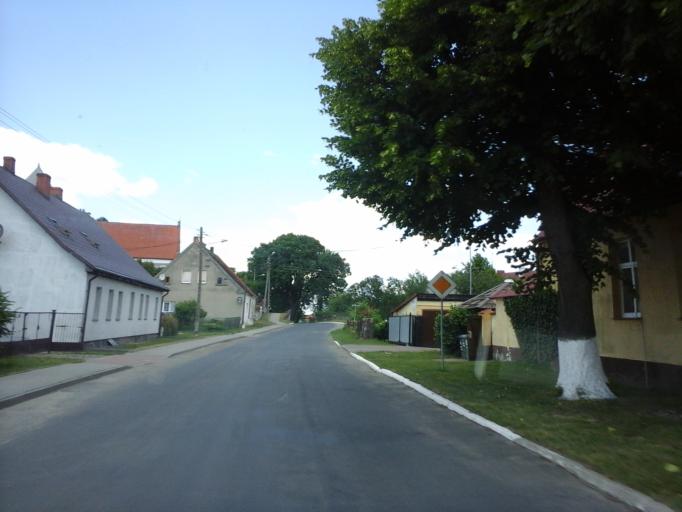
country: PL
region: West Pomeranian Voivodeship
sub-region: Powiat choszczenski
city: Recz
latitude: 53.1846
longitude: 15.5876
